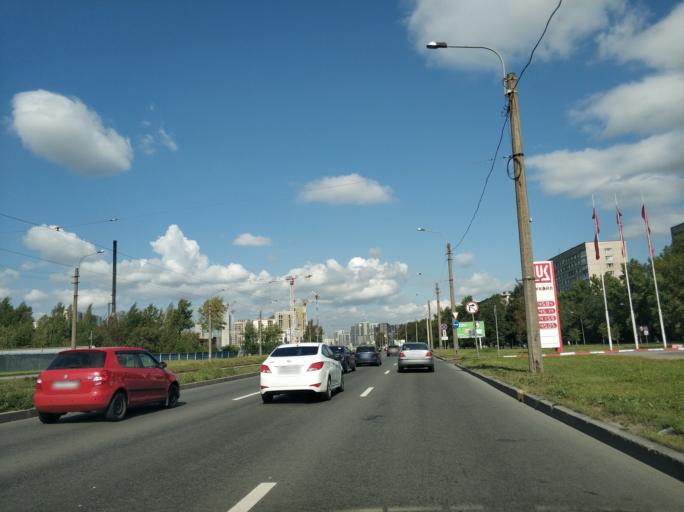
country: RU
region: St.-Petersburg
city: Obukhovo
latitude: 59.8949
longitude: 30.4621
